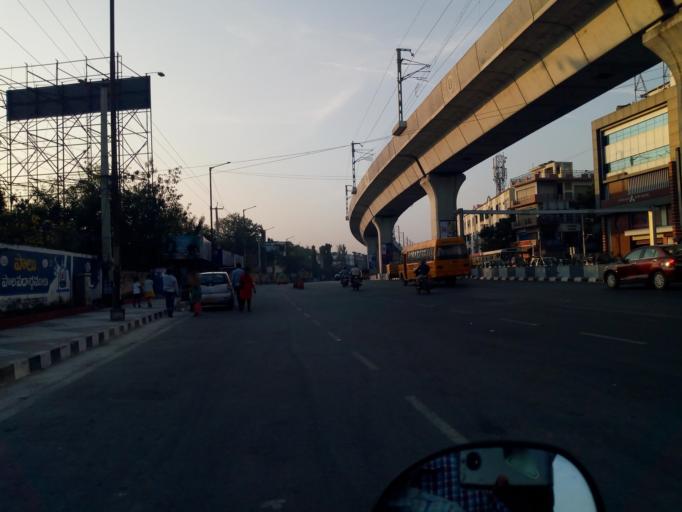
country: IN
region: Telangana
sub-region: Hyderabad
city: Malkajgiri
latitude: 17.4284
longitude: 78.5278
